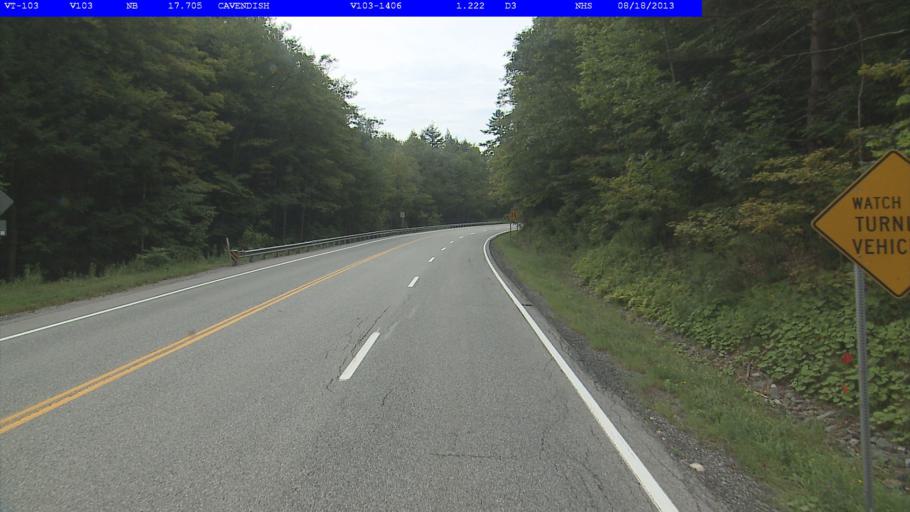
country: US
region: Vermont
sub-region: Windsor County
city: Chester
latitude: 43.3644
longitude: -72.6356
